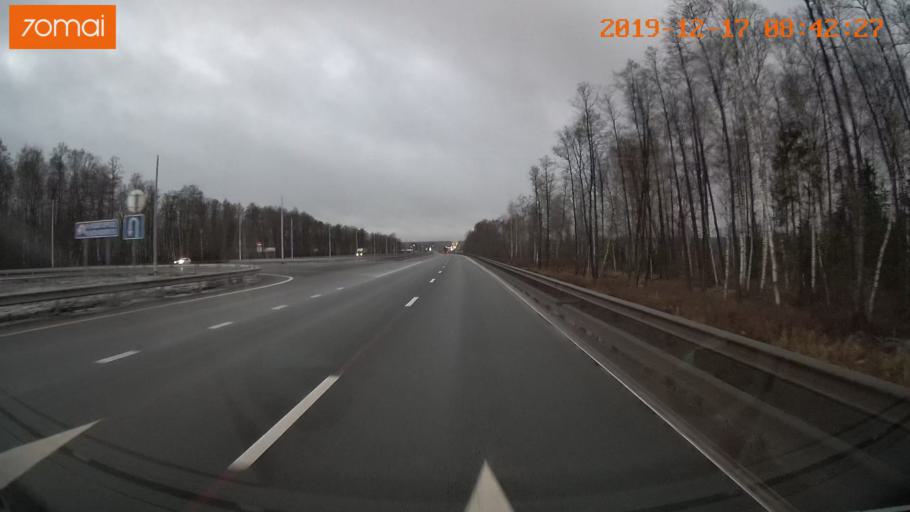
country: RU
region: Vladimir
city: Kosterevo
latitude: 55.9638
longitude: 39.7424
